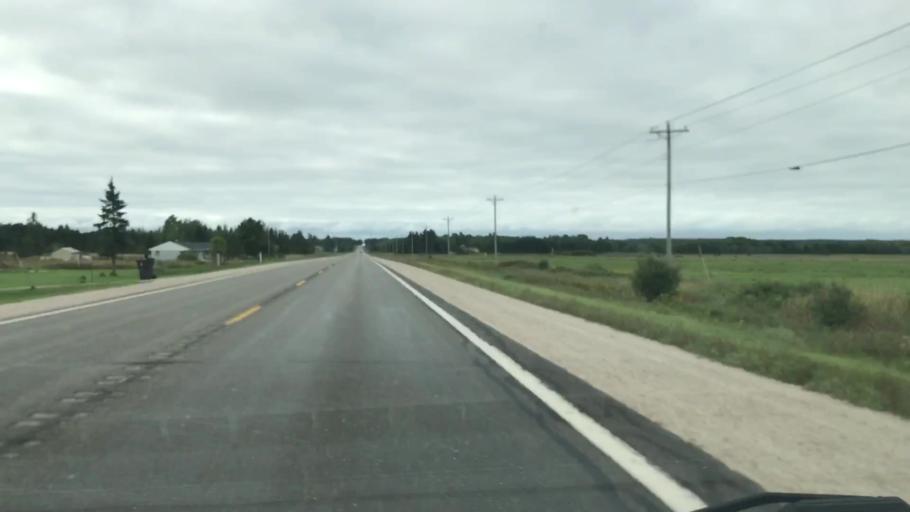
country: US
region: Michigan
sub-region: Luce County
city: Newberry
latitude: 46.1466
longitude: -85.5713
